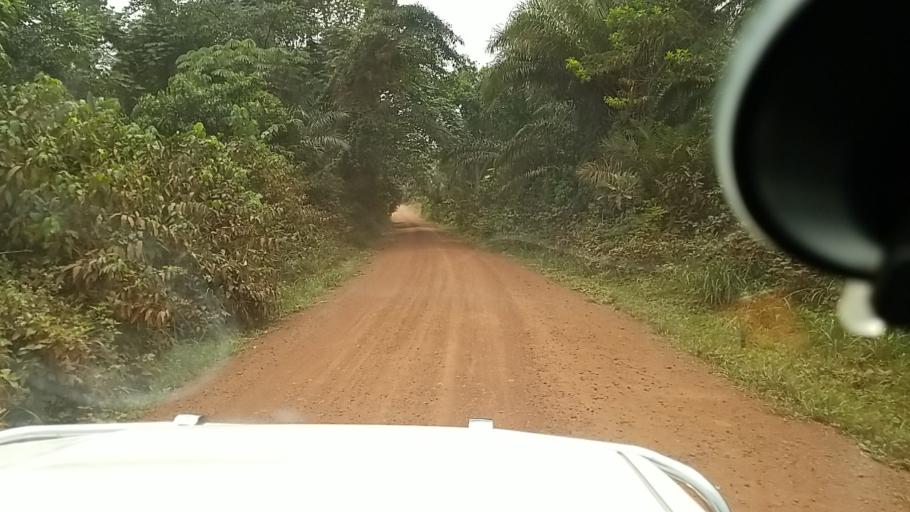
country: CD
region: Equateur
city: Libenge
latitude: 3.7459
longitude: 18.7856
